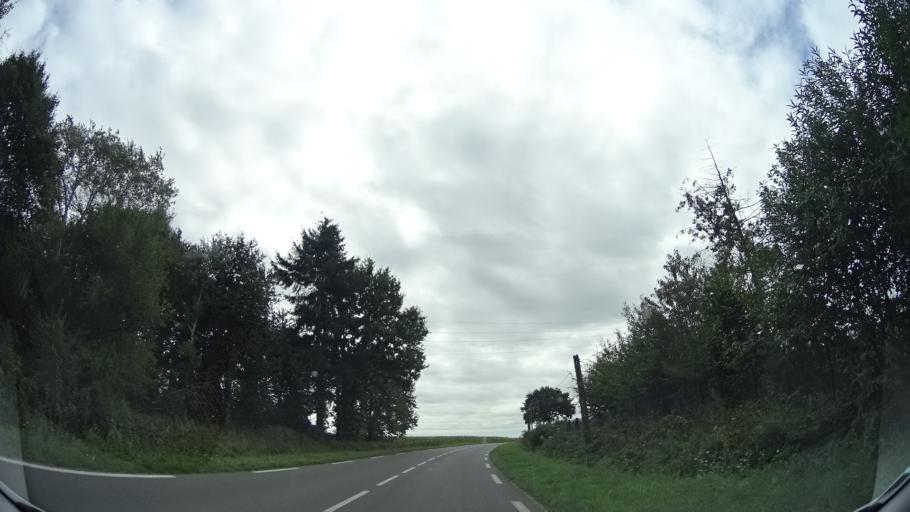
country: FR
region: Brittany
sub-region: Departement d'Ille-et-Vilaine
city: Hede-Bazouges
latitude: 48.2614
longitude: -1.8344
